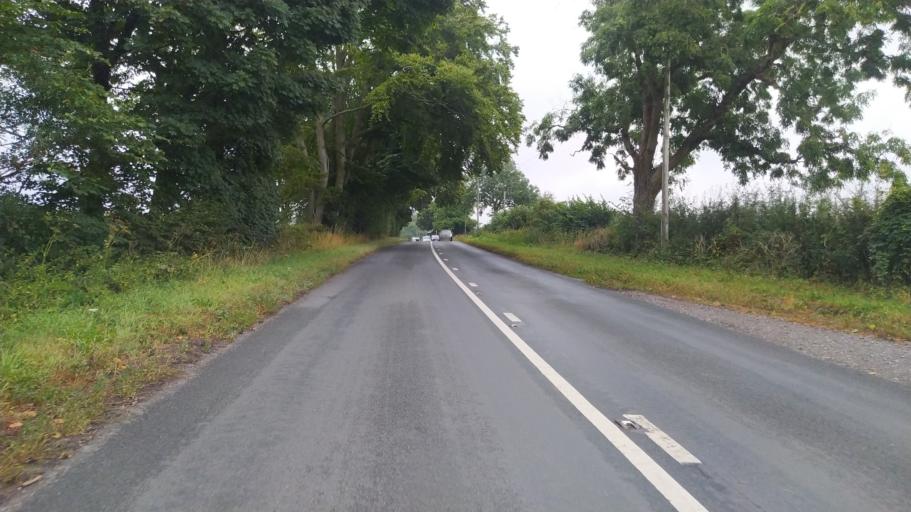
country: GB
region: England
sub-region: Wiltshire
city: Ansty
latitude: 51.0270
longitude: -2.0820
